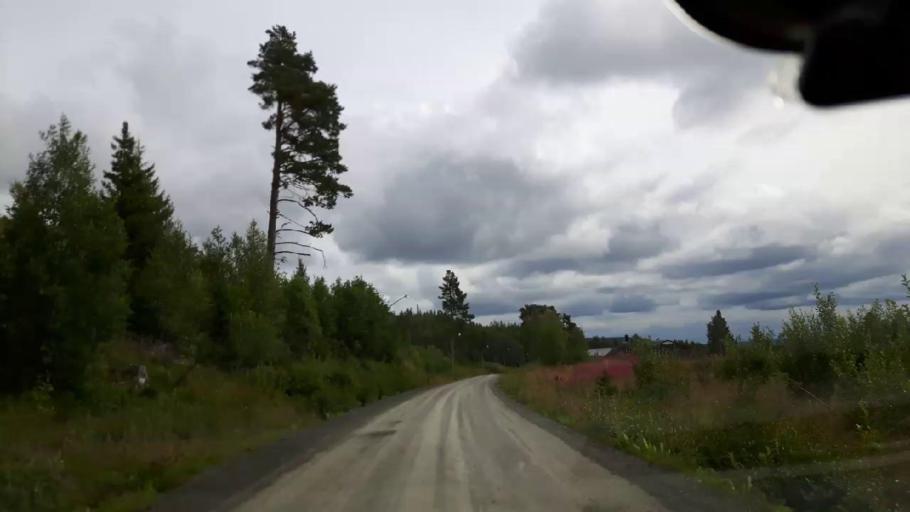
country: SE
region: Jaemtland
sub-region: Krokoms Kommun
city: Valla
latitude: 63.6243
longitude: 14.0485
